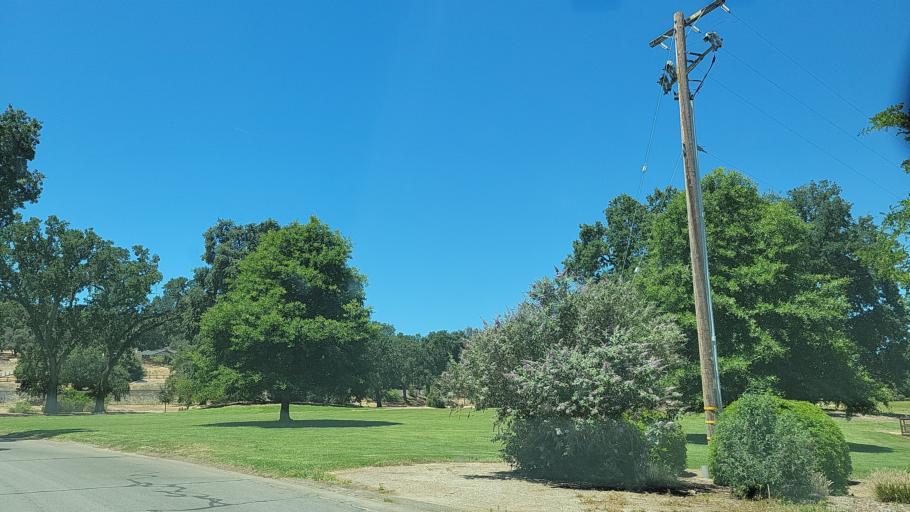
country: US
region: California
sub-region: San Luis Obispo County
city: Atascadero
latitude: 35.5125
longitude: -120.6702
